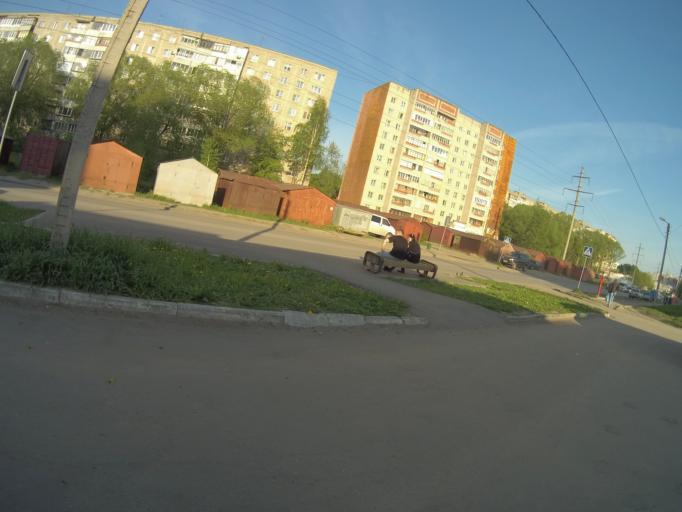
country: RU
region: Vladimir
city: Kommunar
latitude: 56.1691
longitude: 40.4541
